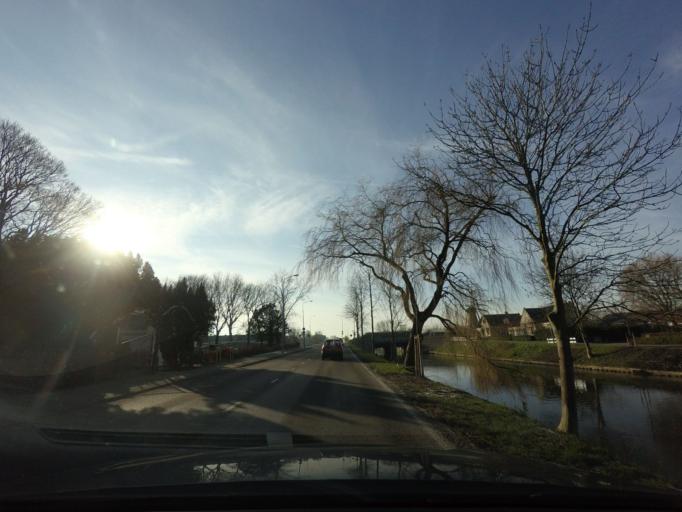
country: NL
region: North Holland
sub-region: Gemeente Haarlemmermeer
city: Hoofddorp
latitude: 52.3019
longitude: 4.6878
